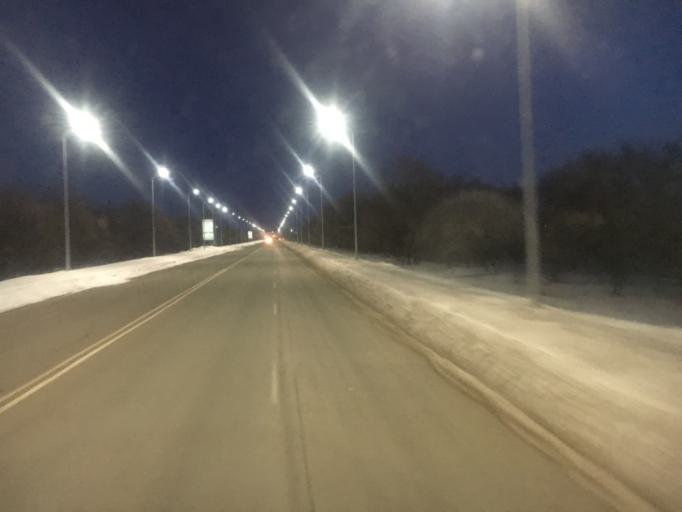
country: KZ
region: Batys Qazaqstan
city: Oral
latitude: 51.1592
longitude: 51.5315
